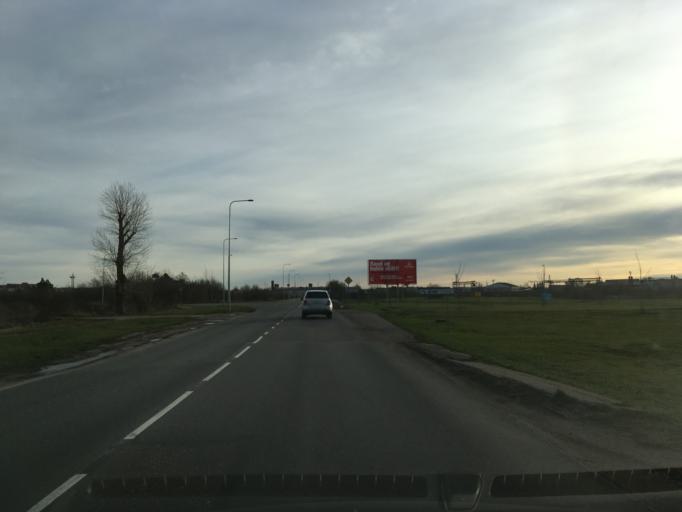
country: EE
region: Ida-Virumaa
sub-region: Narva linn
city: Narva
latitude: 59.3664
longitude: 28.1645
